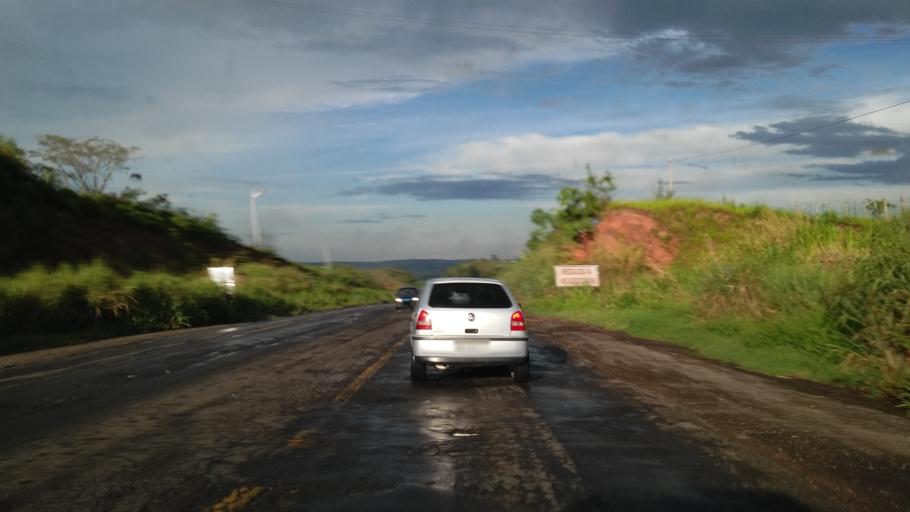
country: BR
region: Sao Paulo
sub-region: Marilia
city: Marilia
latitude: -22.1278
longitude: -49.9371
